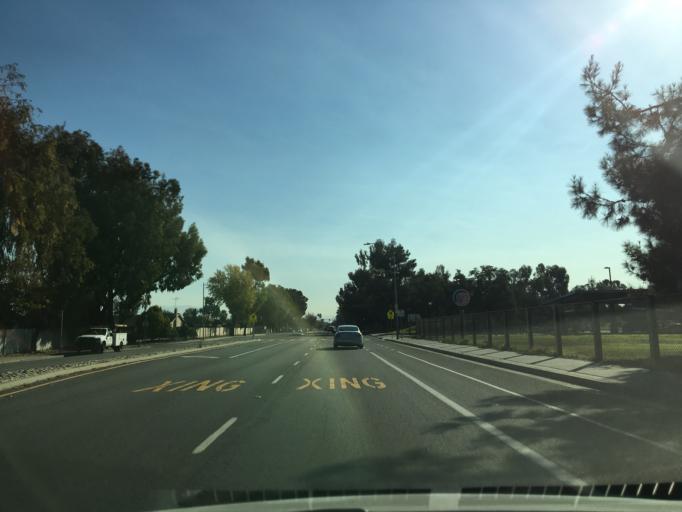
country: US
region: California
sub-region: Santa Clara County
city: Alum Rock
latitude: 37.3692
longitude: -121.8542
